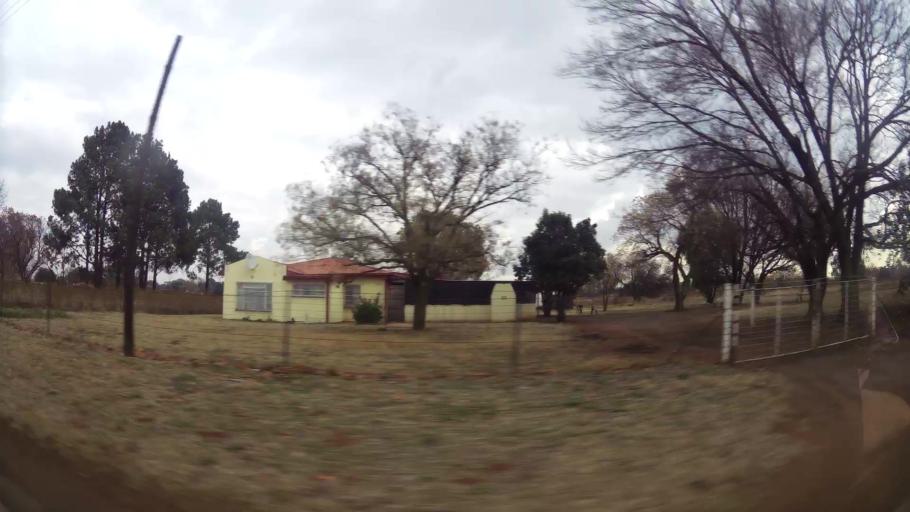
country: ZA
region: Gauteng
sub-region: Sedibeng District Municipality
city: Meyerton
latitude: -26.5820
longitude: 28.0009
